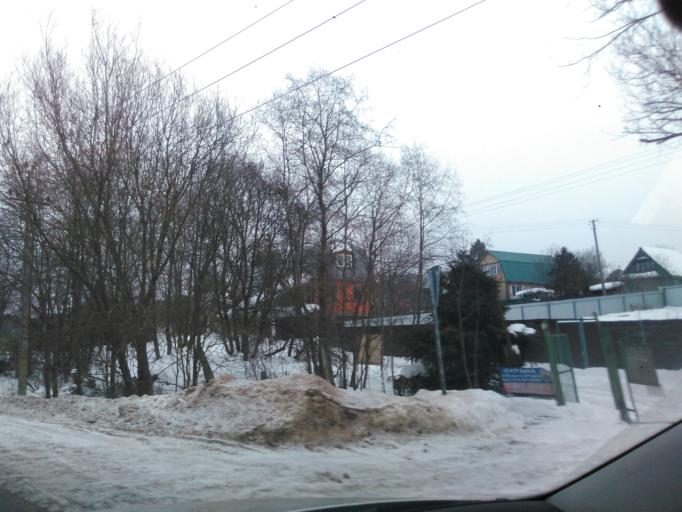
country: RU
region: Moskovskaya
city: Dedenevo
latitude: 56.2634
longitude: 37.5668
